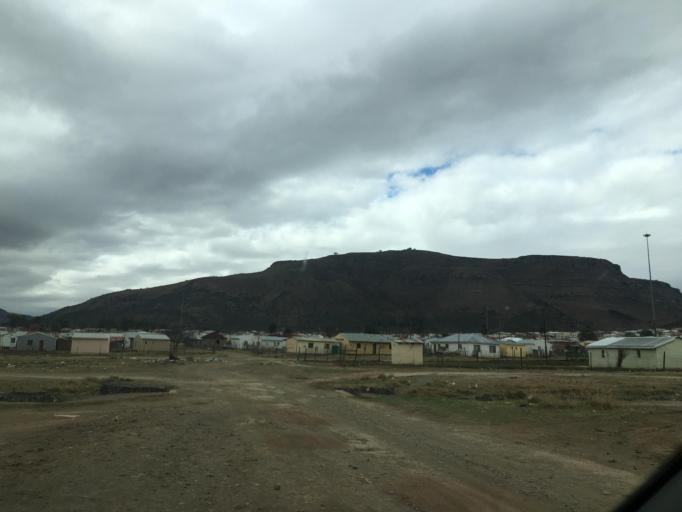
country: ZA
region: Eastern Cape
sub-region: Chris Hani District Municipality
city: Cala
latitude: -31.5365
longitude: 27.6993
